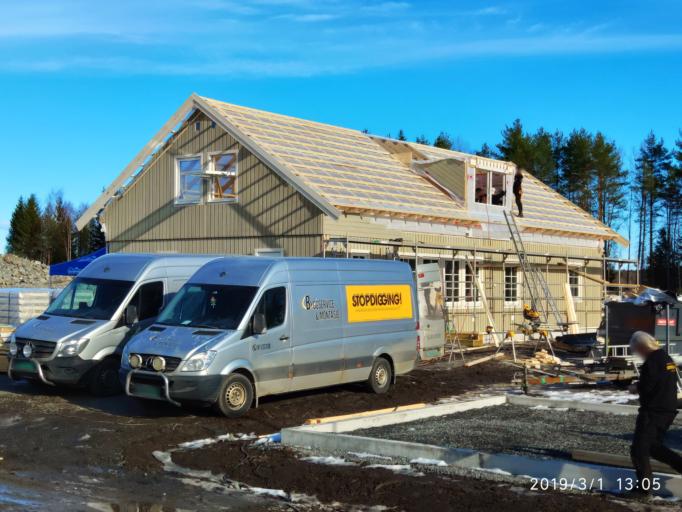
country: NO
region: Akershus
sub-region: Nes
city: Arnes
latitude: 60.1706
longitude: 11.5499
